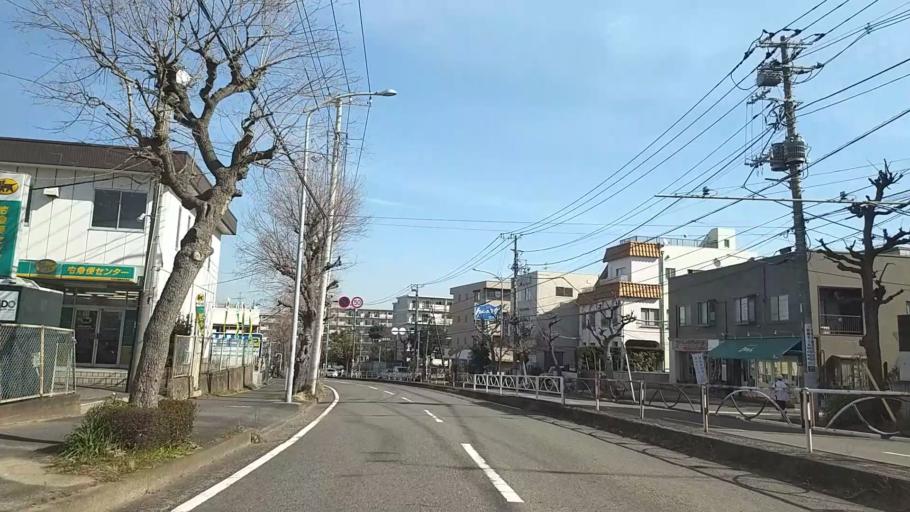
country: JP
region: Kanagawa
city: Kamakura
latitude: 35.3683
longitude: 139.5828
